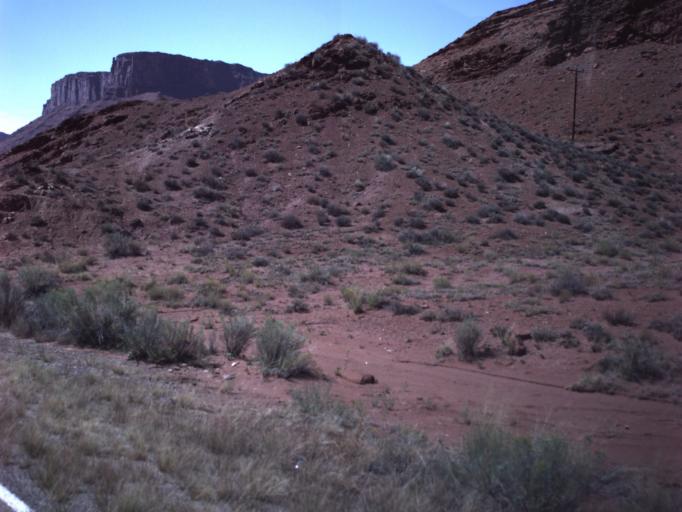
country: US
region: Utah
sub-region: Grand County
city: Moab
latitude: 38.7054
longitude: -109.3842
